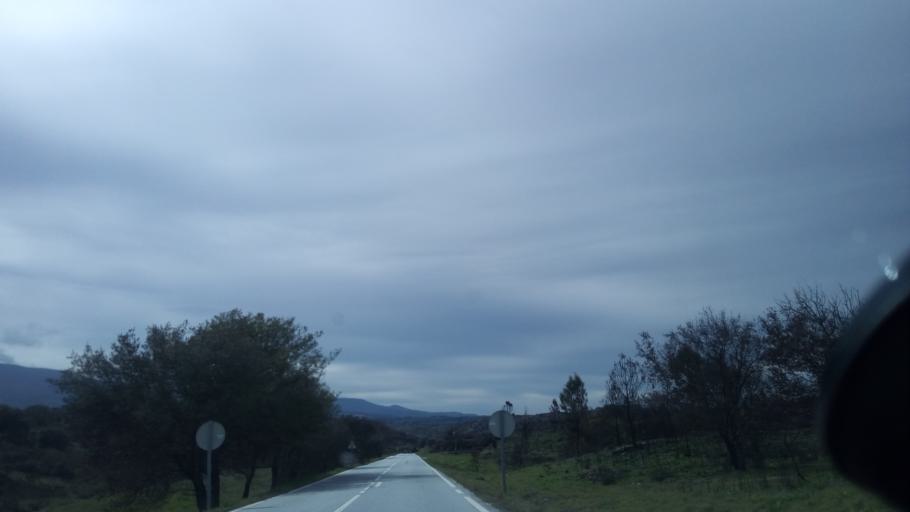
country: PT
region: Guarda
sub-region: Fornos de Algodres
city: Fornos de Algodres
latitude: 40.5739
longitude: -7.5505
